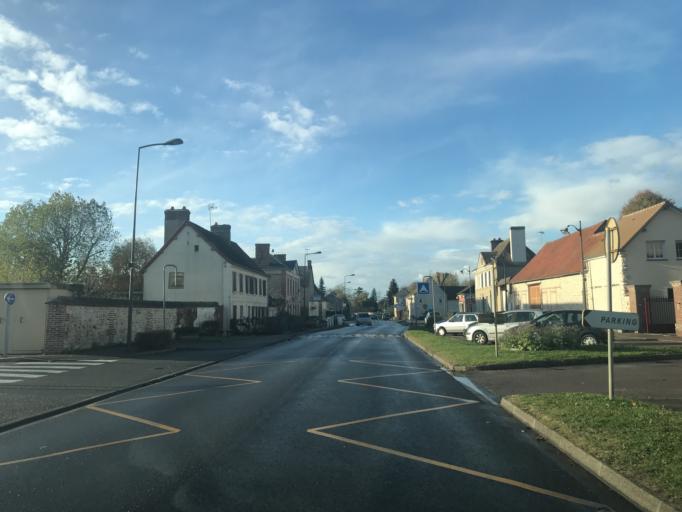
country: FR
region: Haute-Normandie
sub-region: Departement de l'Eure
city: Saint-Aubin-sur-Gaillon
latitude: 49.0958
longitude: 1.2803
